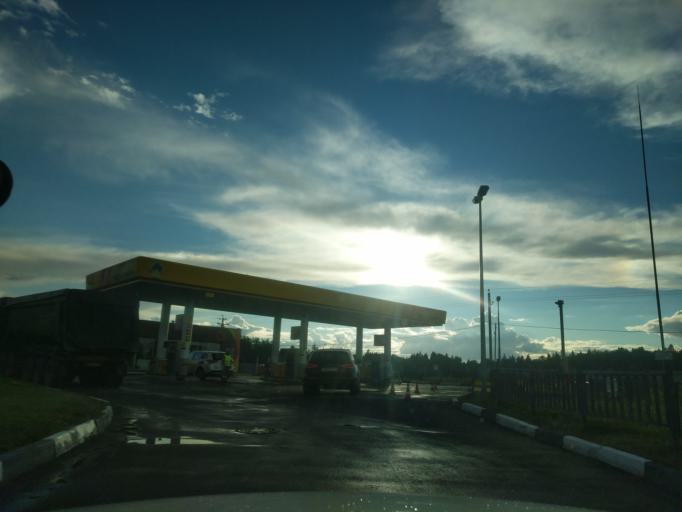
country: RU
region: Moskovskaya
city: Ashukino
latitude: 56.1822
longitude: 38.0282
